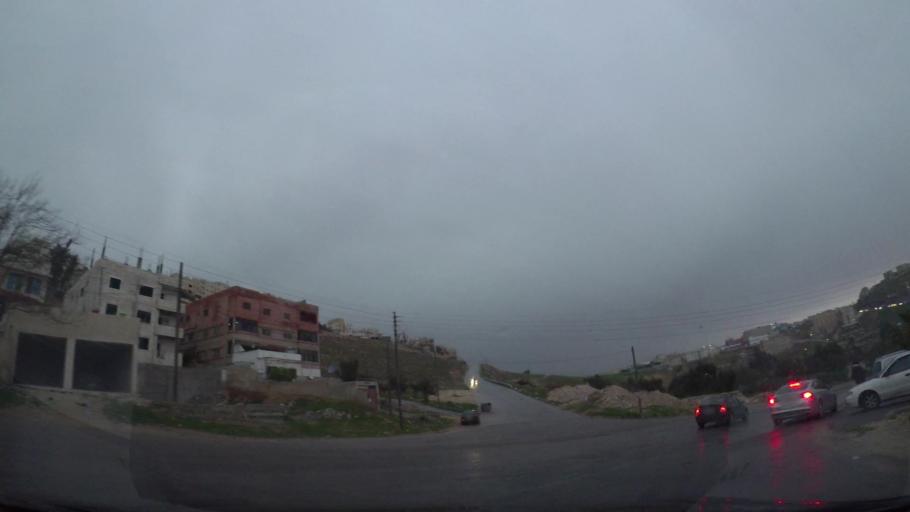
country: JO
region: Amman
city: Amman
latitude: 31.9929
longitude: 35.9789
